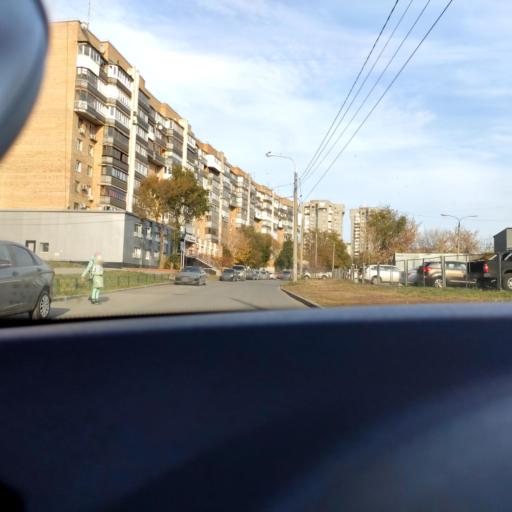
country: RU
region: Samara
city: Samara
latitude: 53.1915
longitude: 50.1362
